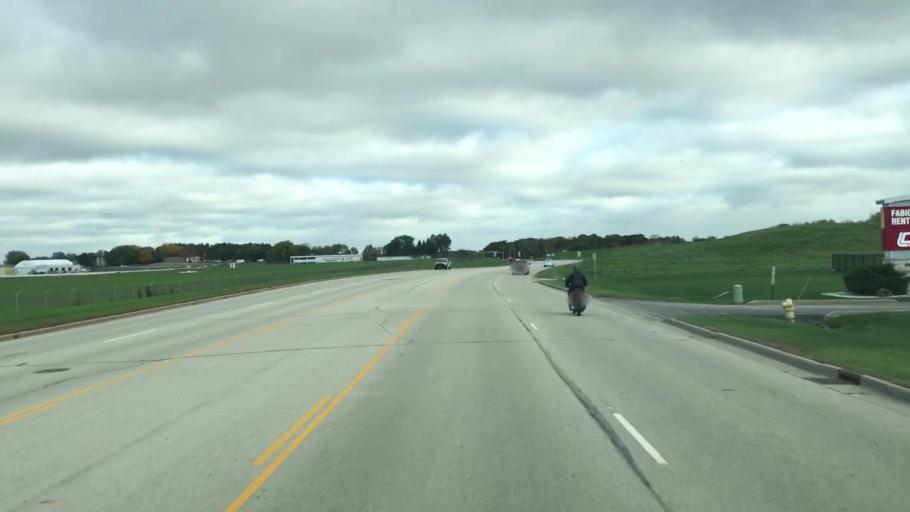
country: US
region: Wisconsin
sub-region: Waukesha County
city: Waukesha
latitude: 43.0372
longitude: -88.2258
